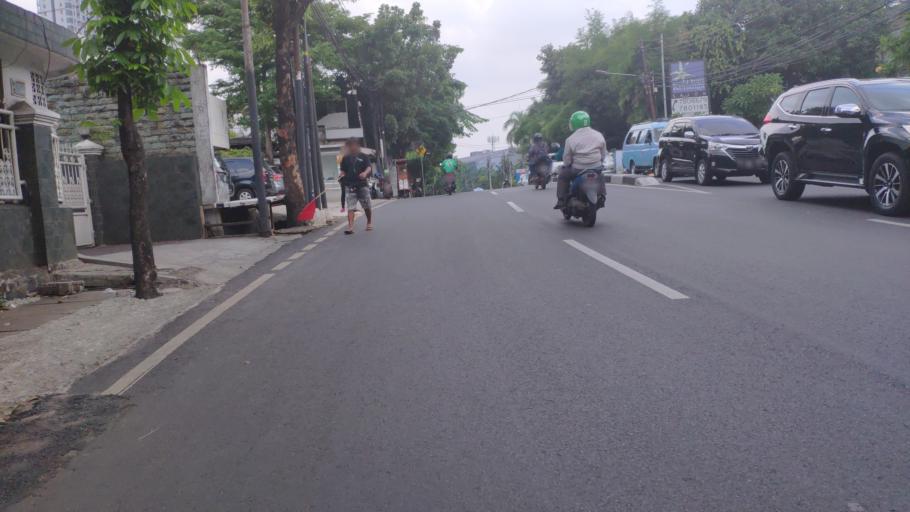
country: ID
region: Jakarta Raya
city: Jakarta
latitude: -6.2774
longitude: 106.8264
